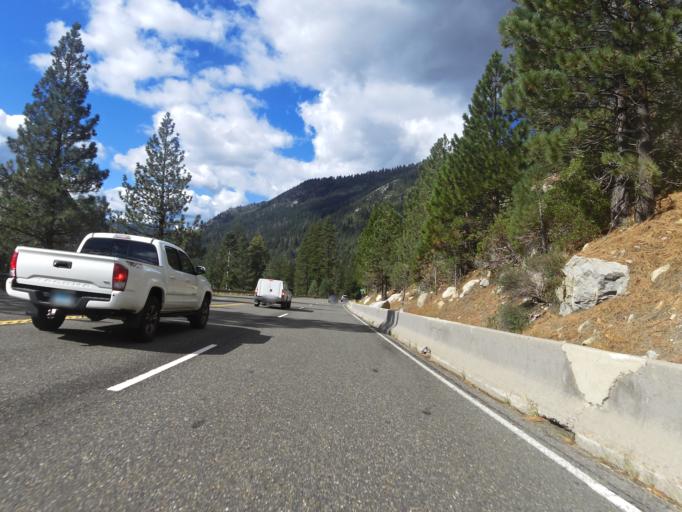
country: US
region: California
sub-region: El Dorado County
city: South Lake Tahoe
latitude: 38.8098
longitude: -120.1299
